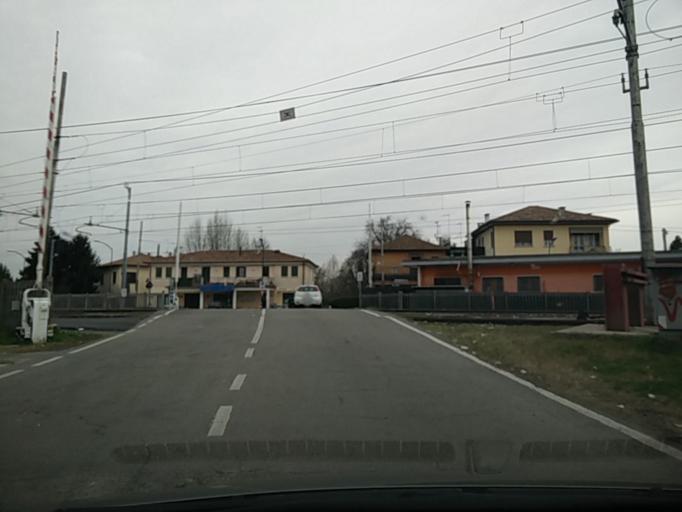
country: IT
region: Veneto
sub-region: Provincia di Treviso
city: Treviso
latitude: 45.6579
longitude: 12.2348
